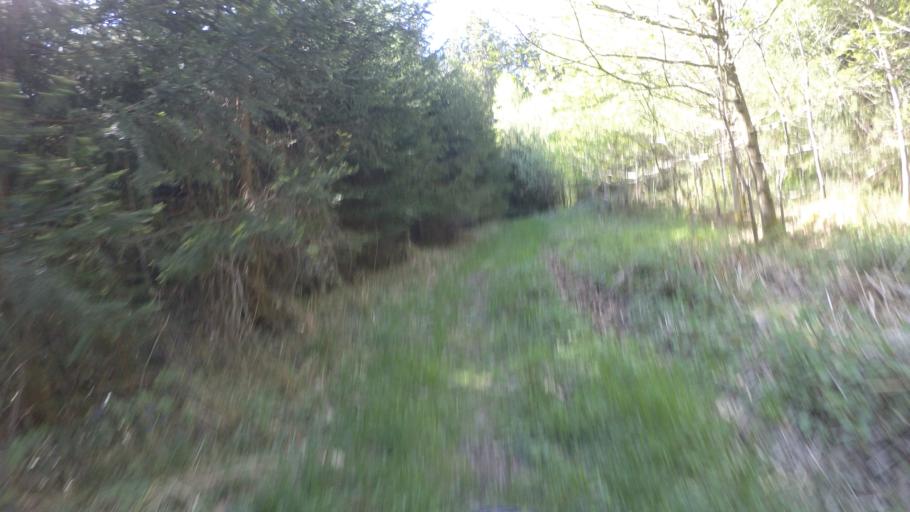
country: DE
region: Bavaria
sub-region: Upper Bavaria
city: Chieming
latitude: 47.9492
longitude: 12.5333
